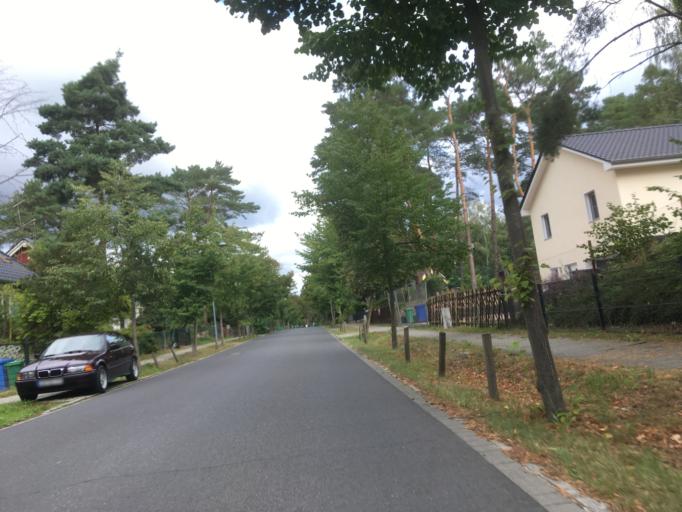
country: DE
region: Brandenburg
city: Wildau
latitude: 52.3125
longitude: 13.7015
